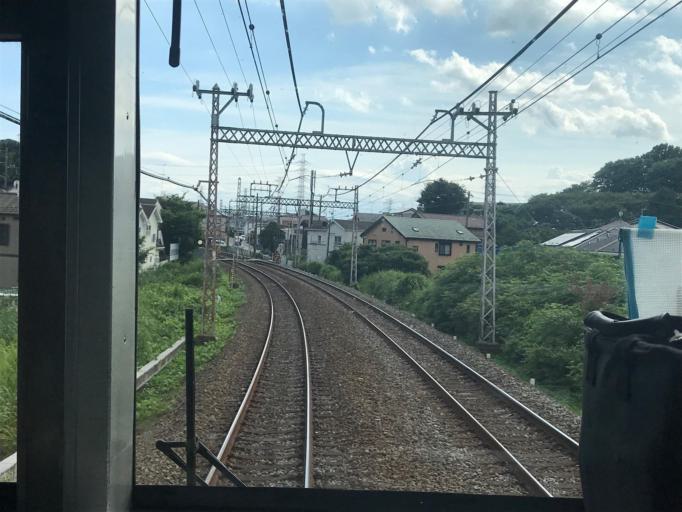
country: JP
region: Kanagawa
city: Atsugi
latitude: 35.4134
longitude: 139.3375
